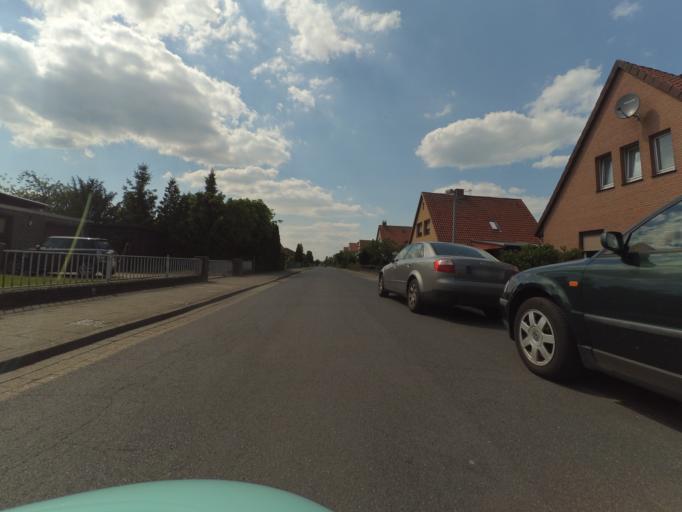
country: DE
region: Lower Saxony
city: Uetze
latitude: 52.4598
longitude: 10.1923
